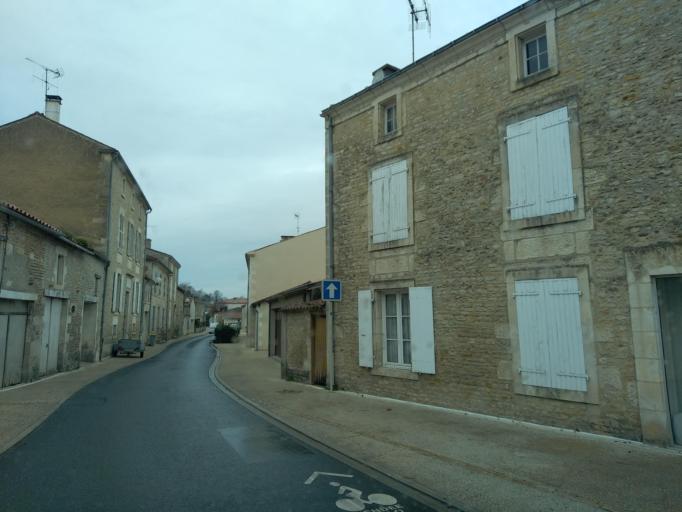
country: FR
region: Pays de la Loire
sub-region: Departement de la Vendee
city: Maillezais
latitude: 46.3726
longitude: -0.7392
